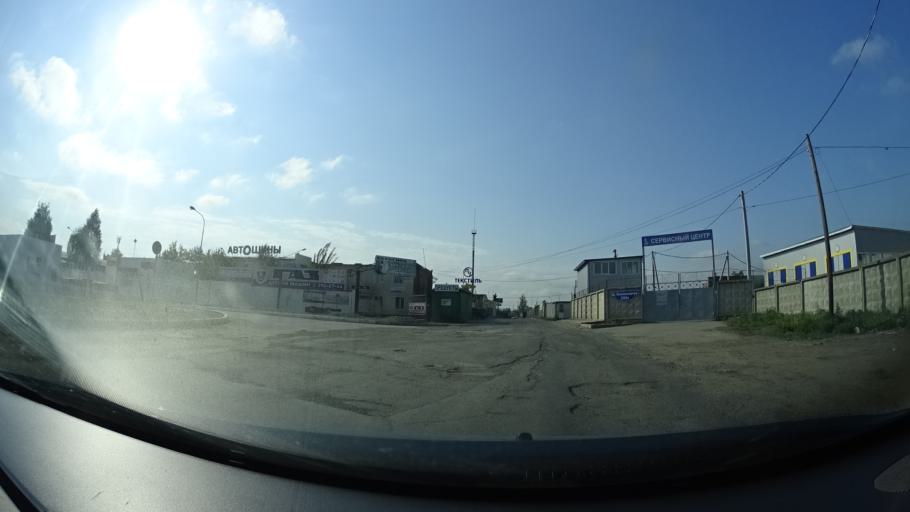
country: RU
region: Perm
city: Kondratovo
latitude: 57.9512
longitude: 56.1059
